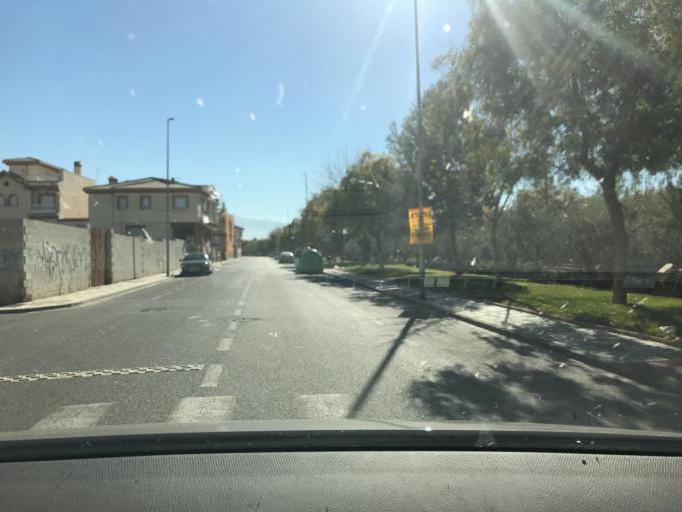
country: ES
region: Andalusia
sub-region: Provincia de Granada
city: Maracena
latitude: 37.2080
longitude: -3.6456
